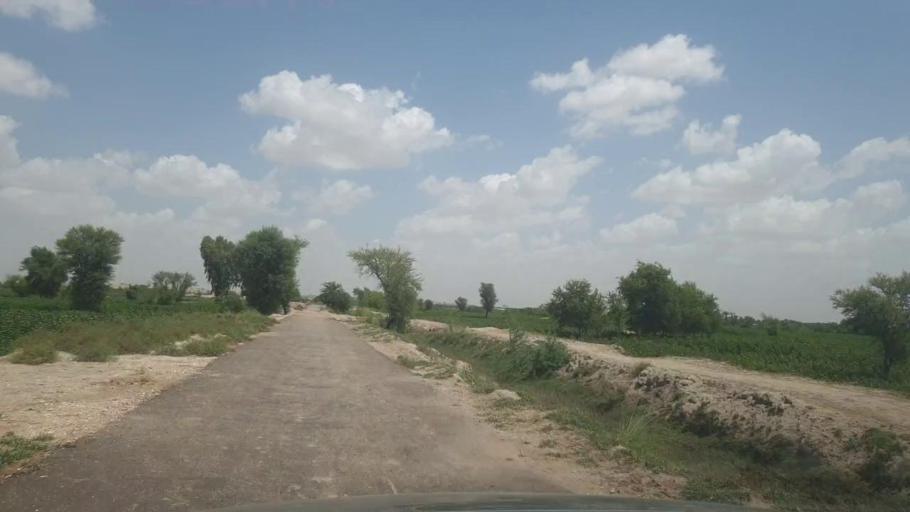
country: PK
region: Sindh
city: Kot Diji
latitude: 27.2341
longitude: 69.0377
